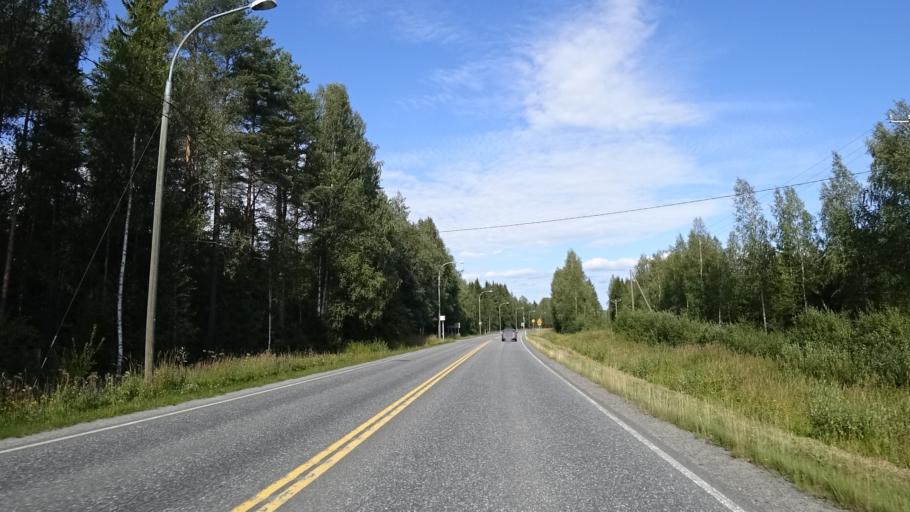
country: FI
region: North Karelia
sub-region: Joensuu
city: Eno
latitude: 62.7933
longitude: 30.0877
